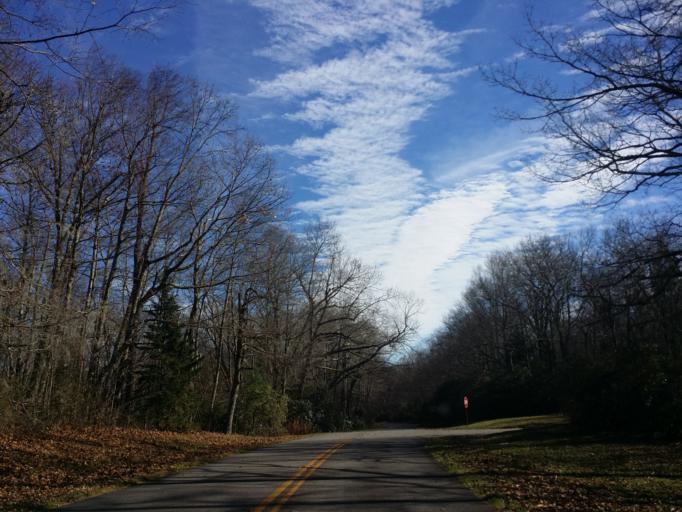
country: US
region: North Carolina
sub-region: Mitchell County
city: Spruce Pine
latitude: 35.8039
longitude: -82.1514
